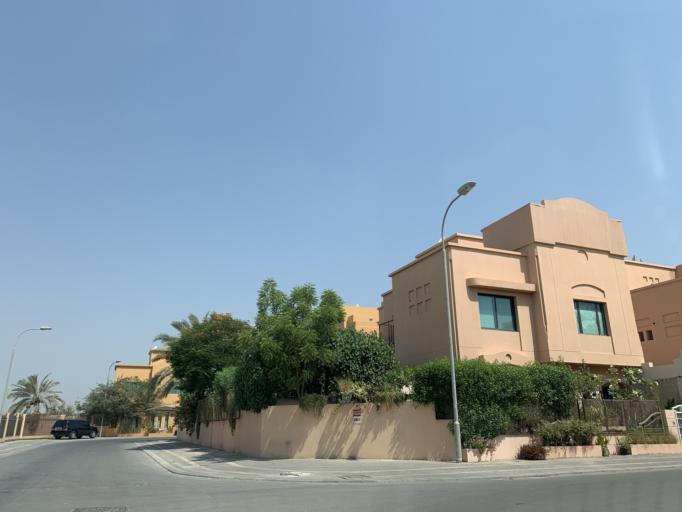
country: BH
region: Manama
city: Jidd Hafs
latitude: 26.2108
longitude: 50.5211
